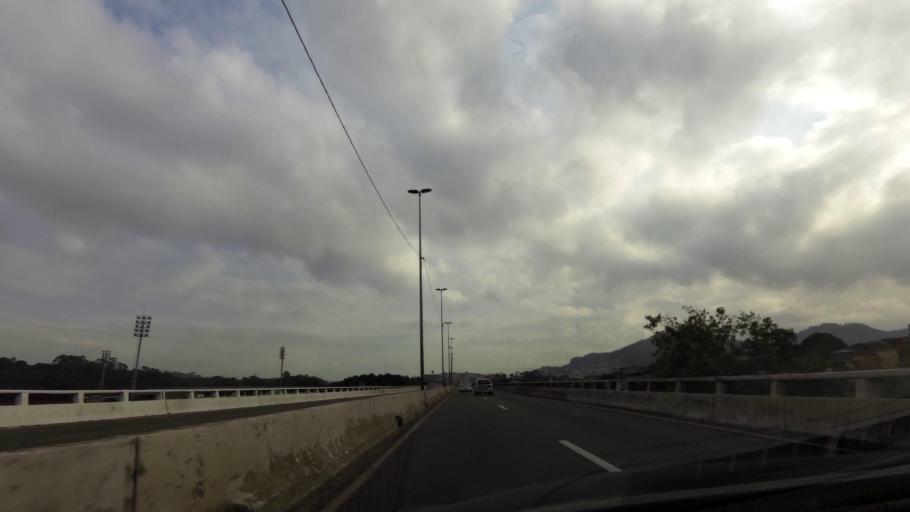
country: BR
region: Espirito Santo
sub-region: Vitoria
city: Vitoria
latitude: -20.3358
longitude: -40.3547
